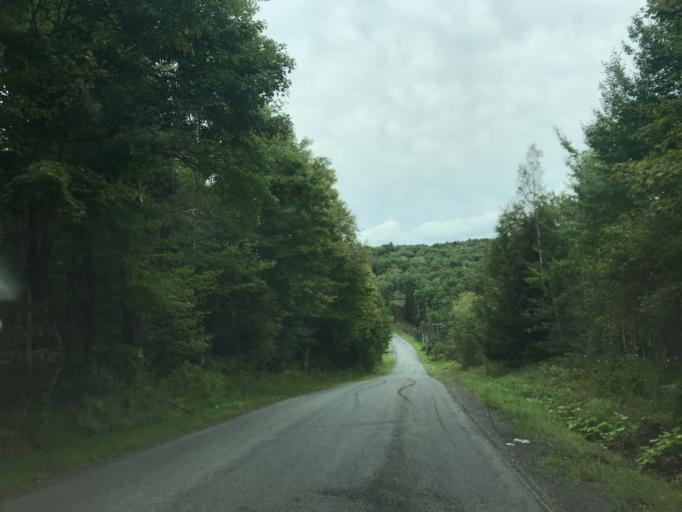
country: US
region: New York
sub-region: Delaware County
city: Stamford
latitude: 42.5332
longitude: -74.6283
